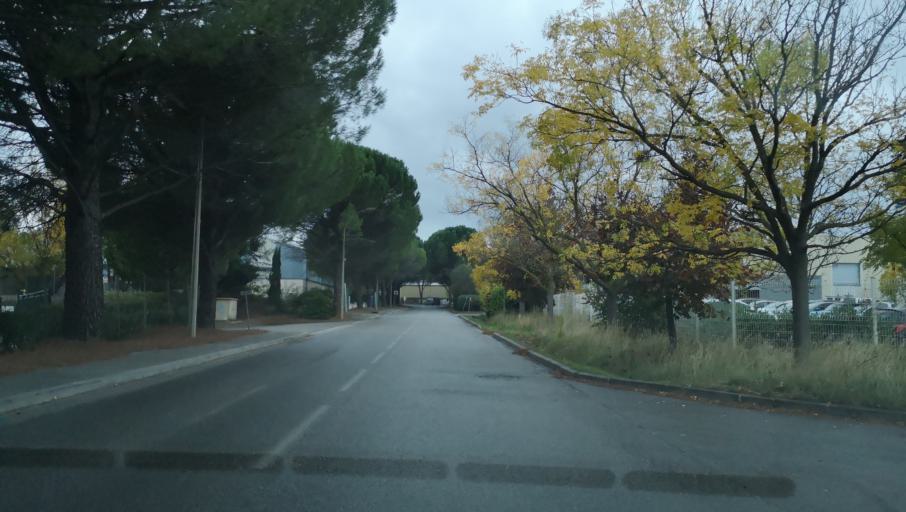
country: FR
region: Provence-Alpes-Cote d'Azur
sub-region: Departement des Bouches-du-Rhone
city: Rousset
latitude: 43.4705
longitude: 5.6085
